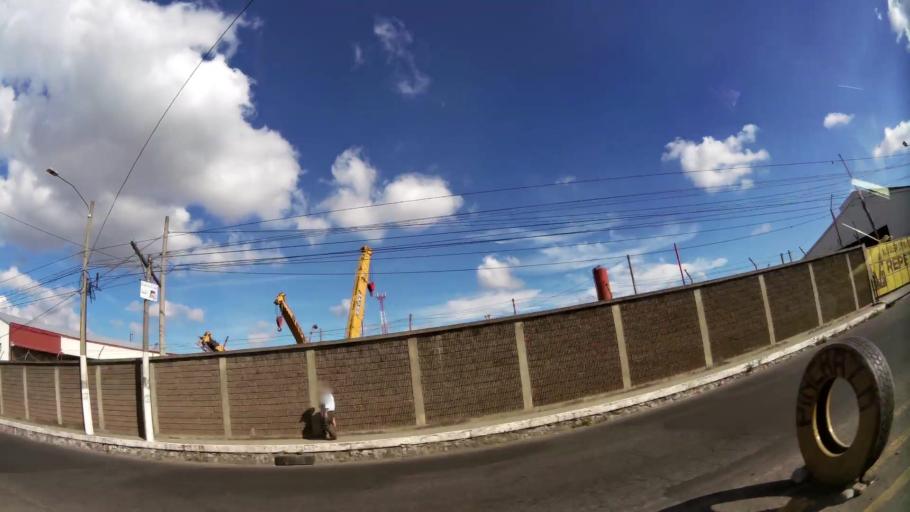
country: GT
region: Guatemala
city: Villa Nueva
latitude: 14.5342
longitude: -90.5856
